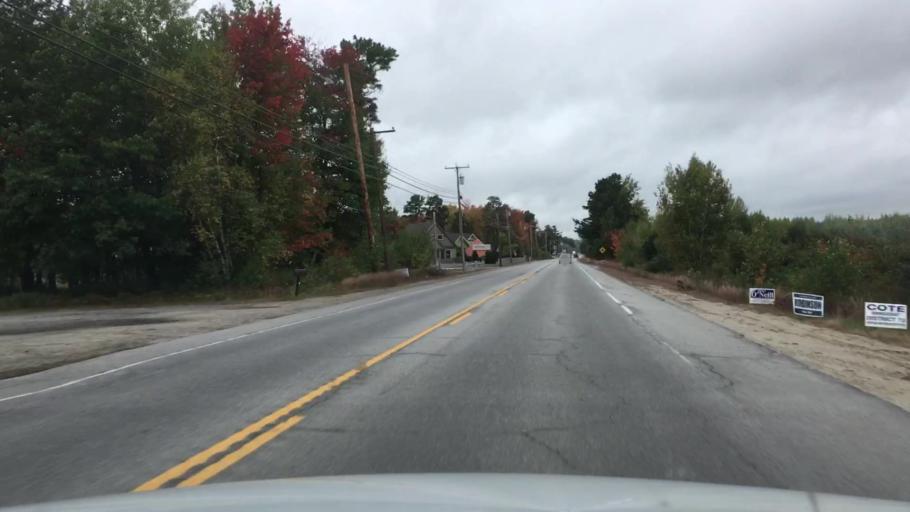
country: US
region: Maine
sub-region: Oxford County
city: Oxford
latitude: 44.1468
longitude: -70.4805
